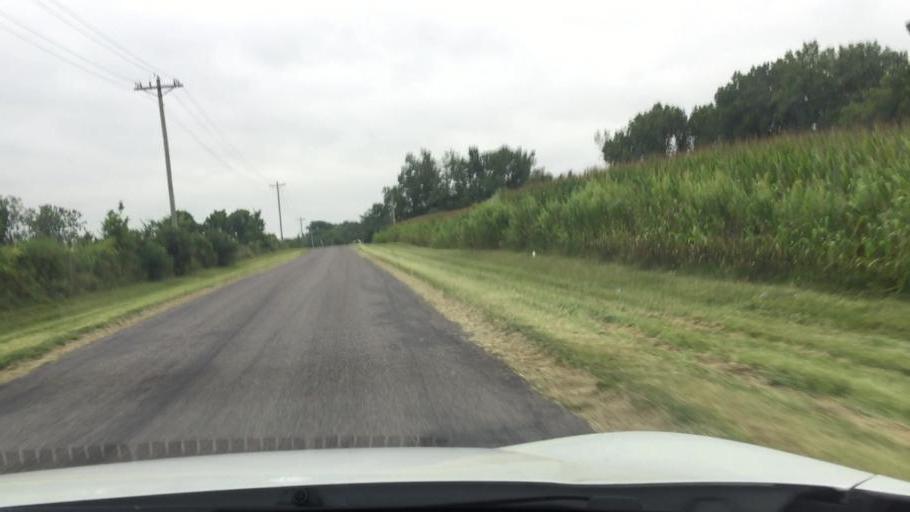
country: US
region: Ohio
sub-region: Champaign County
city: Mechanicsburg
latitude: 40.0554
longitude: -83.5755
